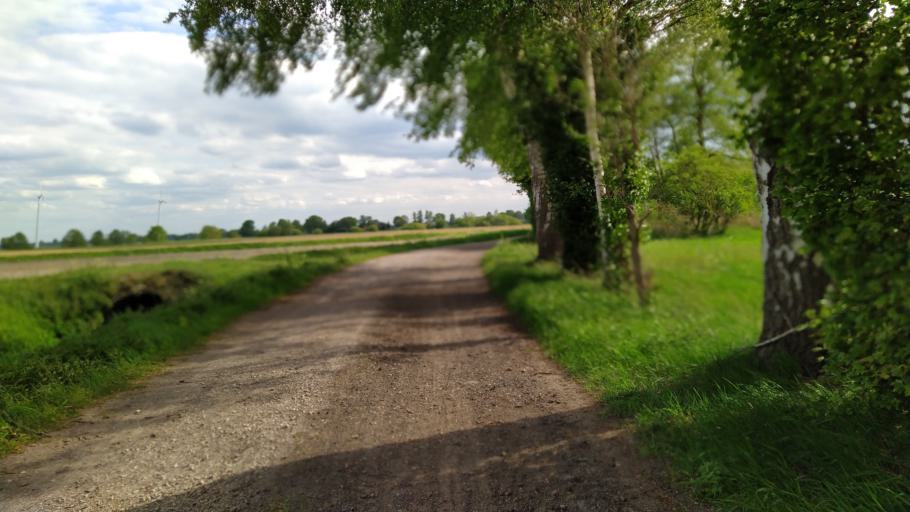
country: DE
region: Lower Saxony
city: Grasberg
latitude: 53.1974
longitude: 9.0293
